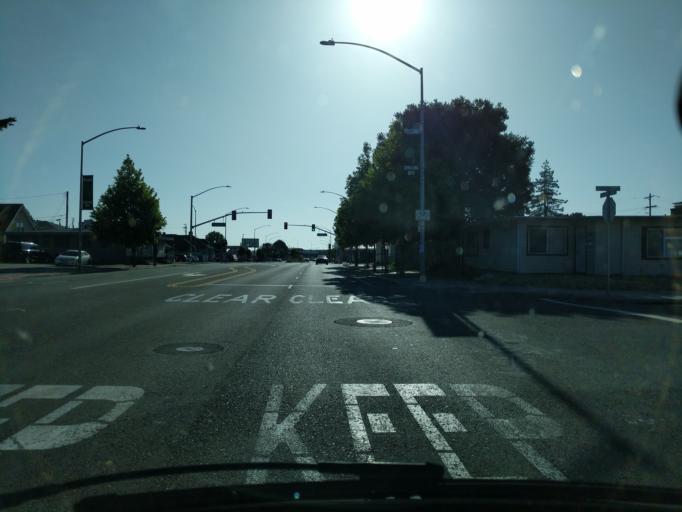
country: US
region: California
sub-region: Alameda County
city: San Lorenzo
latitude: 37.6867
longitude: -122.1265
